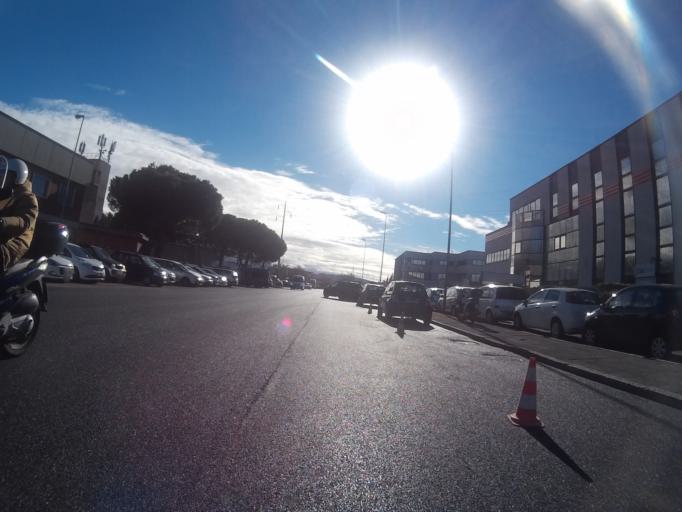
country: IT
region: Tuscany
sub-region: Provincia di Livorno
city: Livorno
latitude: 43.5674
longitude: 10.3413
